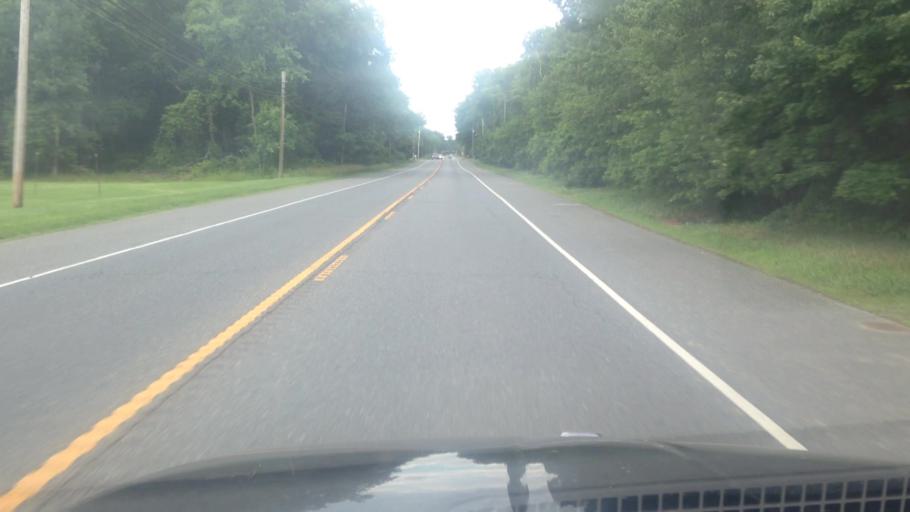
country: US
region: New Jersey
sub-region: Burlington County
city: Leisuretowne
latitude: 39.8289
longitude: -74.7346
